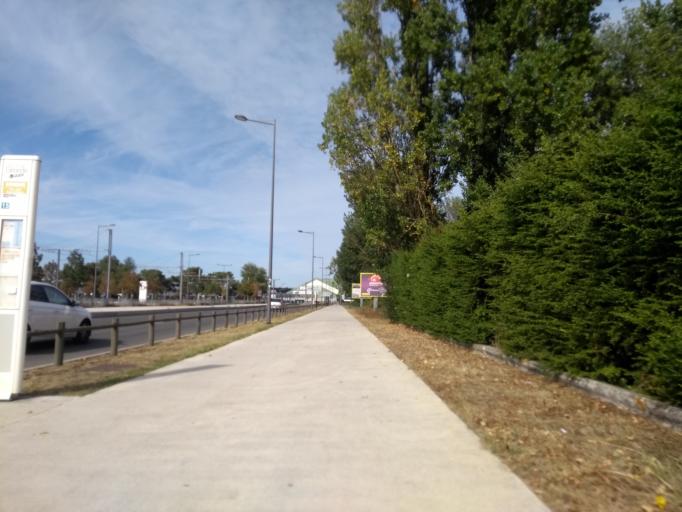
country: FR
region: Aquitaine
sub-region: Departement de la Gironde
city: Le Bouscat
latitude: 44.8938
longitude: -0.5654
